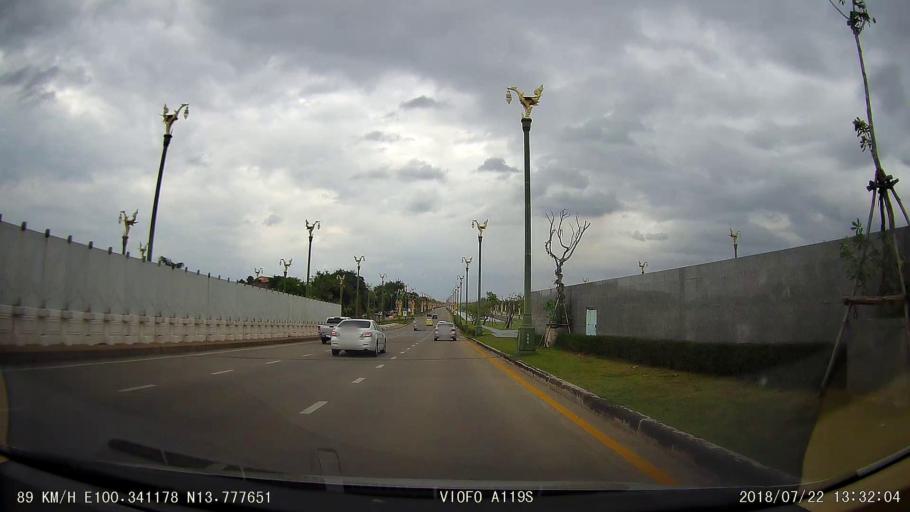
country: TH
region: Bangkok
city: Thawi Watthana
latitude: 13.7777
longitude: 100.3413
